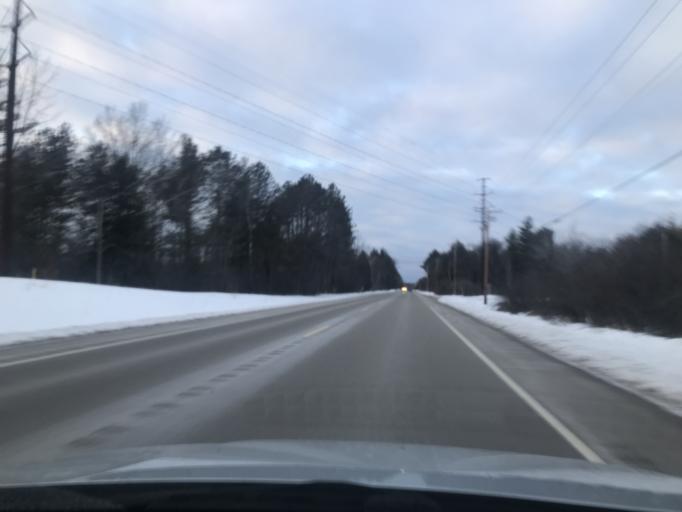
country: US
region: Wisconsin
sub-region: Marinette County
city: Marinette
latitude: 45.1276
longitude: -87.6858
